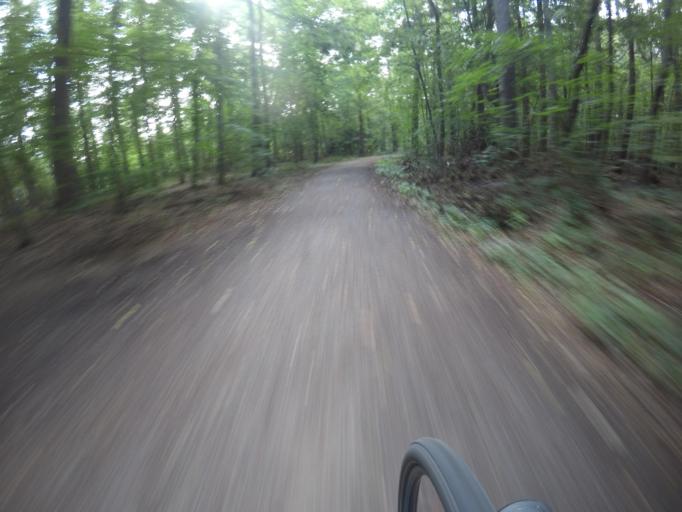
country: DE
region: Baden-Wuerttemberg
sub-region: Regierungsbezirk Stuttgart
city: Ostfildern
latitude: 48.7404
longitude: 9.2512
